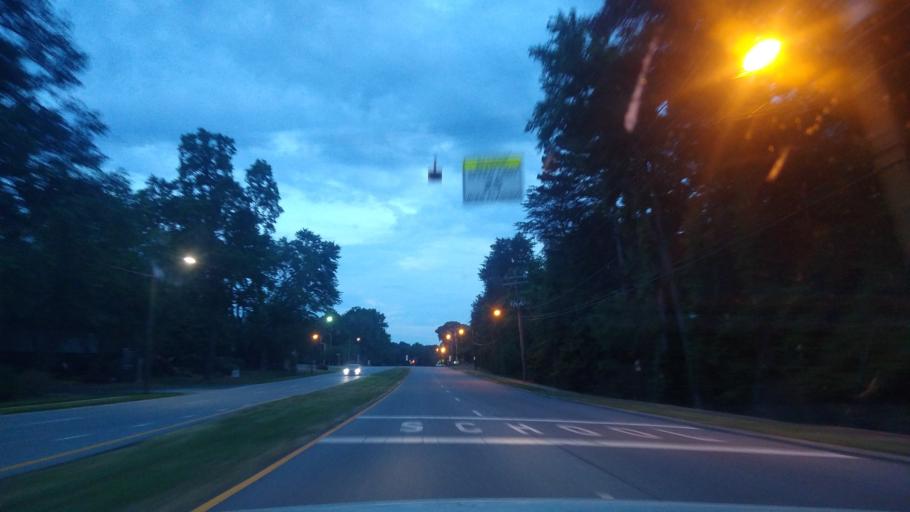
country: US
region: North Carolina
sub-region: Guilford County
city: Greensboro
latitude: 36.1055
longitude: -79.8297
